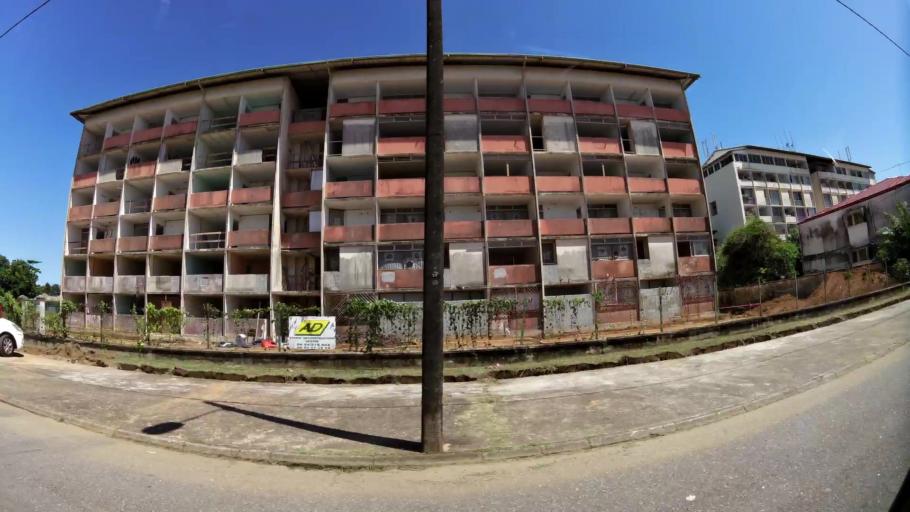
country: GF
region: Guyane
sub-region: Guyane
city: Cayenne
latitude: 4.9439
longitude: -52.3219
